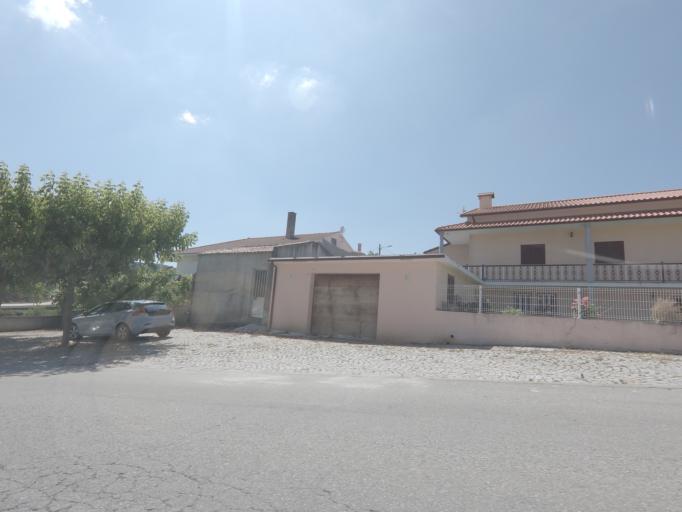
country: PT
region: Viseu
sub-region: Tarouca
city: Tarouca
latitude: 40.9932
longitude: -7.8239
